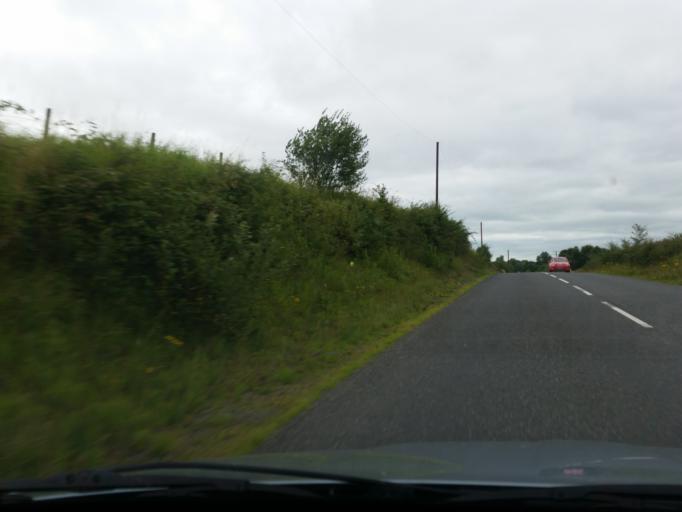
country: GB
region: Northern Ireland
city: Lisnaskea
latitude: 54.2281
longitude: -7.4579
